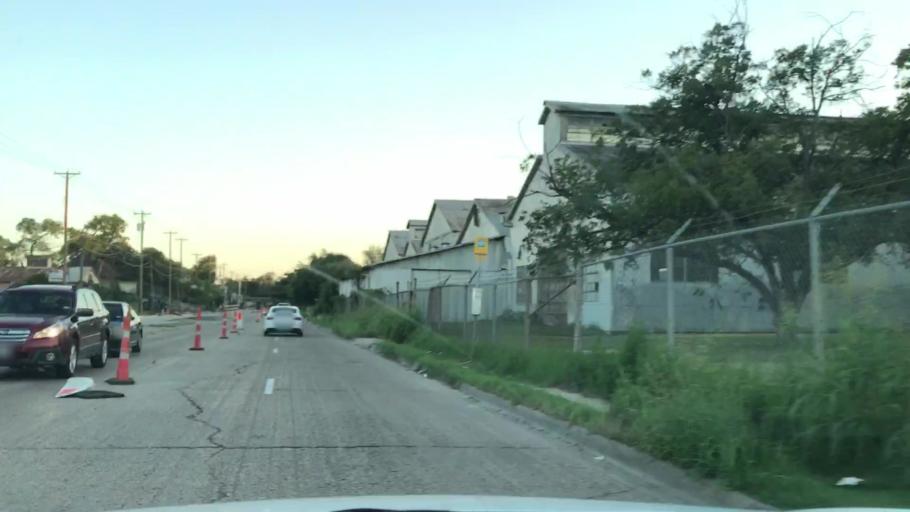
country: US
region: Texas
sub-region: Dallas County
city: Dallas
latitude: 32.7784
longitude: -96.8359
